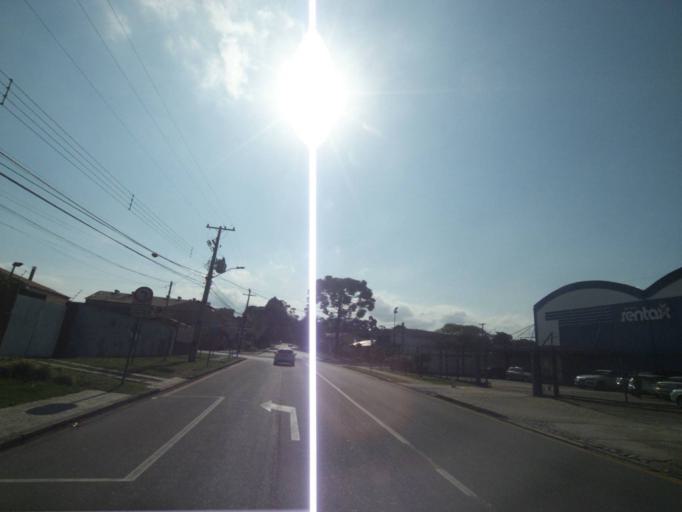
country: BR
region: Parana
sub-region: Pinhais
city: Pinhais
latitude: -25.4091
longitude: -49.2223
